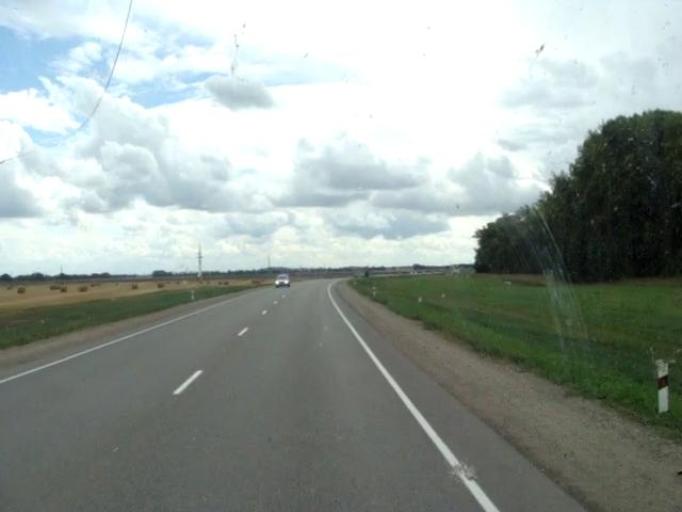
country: RU
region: Altai Krai
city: Shubenka
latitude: 52.6809
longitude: 85.0477
